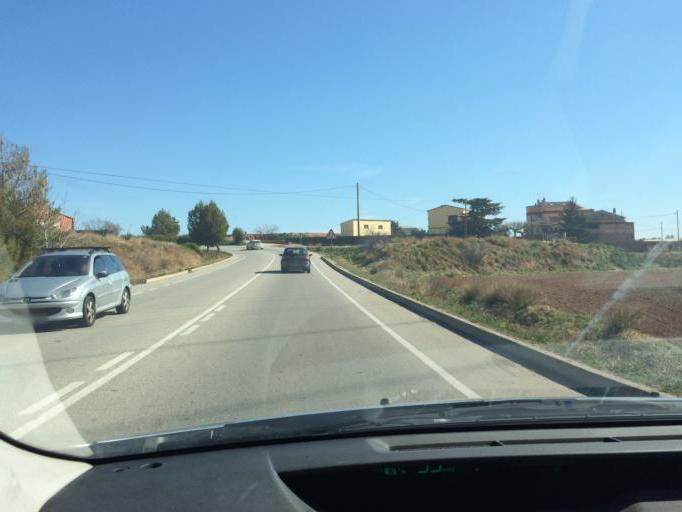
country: ES
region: Catalonia
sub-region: Provincia de Barcelona
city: Manresa
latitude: 41.7427
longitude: 1.8390
